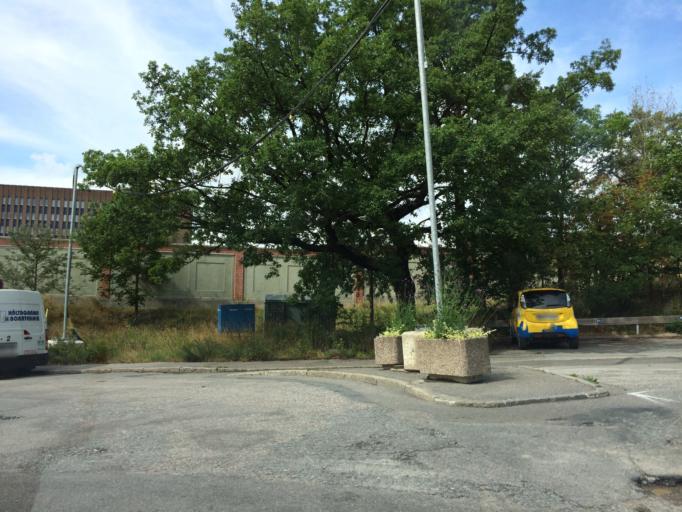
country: SE
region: Stockholm
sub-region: Stockholms Kommun
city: Arsta
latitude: 59.2967
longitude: 18.0064
